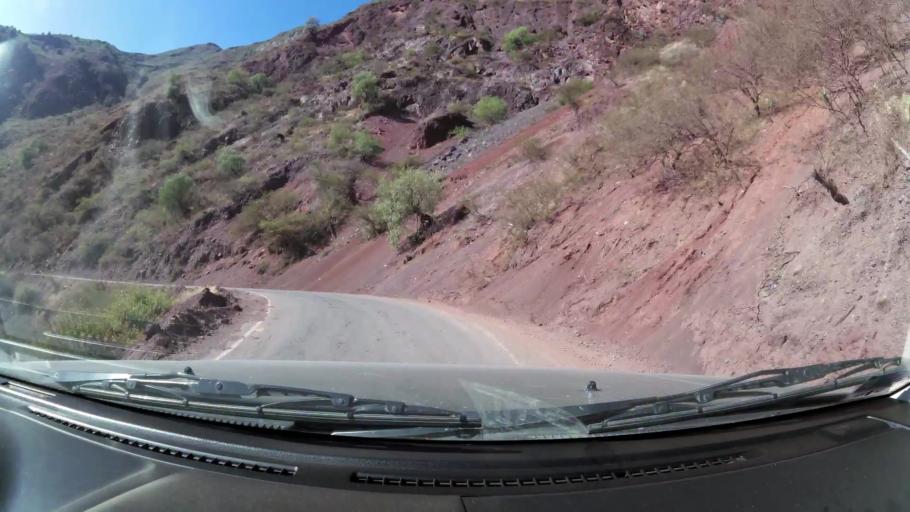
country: PE
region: Huancavelica
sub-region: Provincia de Acobamba
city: Pomacocha
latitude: -12.7887
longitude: -74.4880
